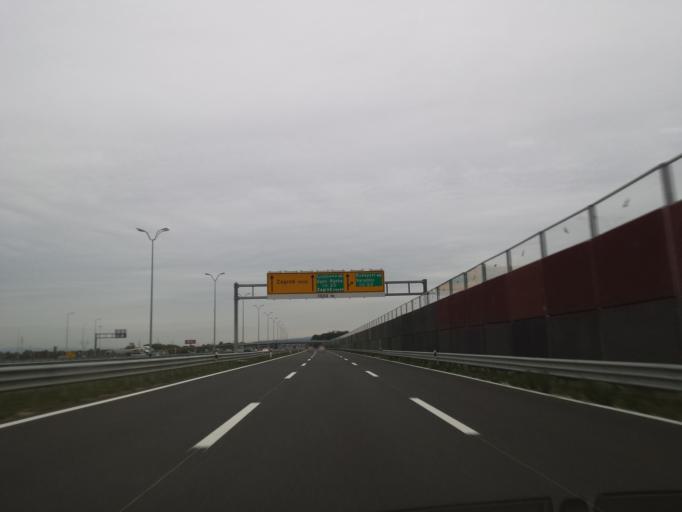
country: HR
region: Grad Zagreb
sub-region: Sesvete
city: Sesvete
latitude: 45.7958
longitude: 16.1531
